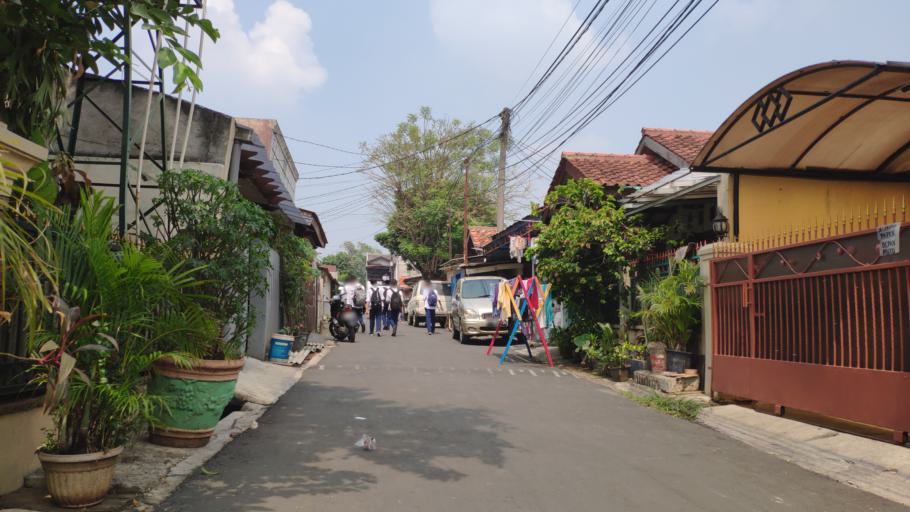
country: ID
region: Banten
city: South Tangerang
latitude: -6.2704
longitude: 106.7735
